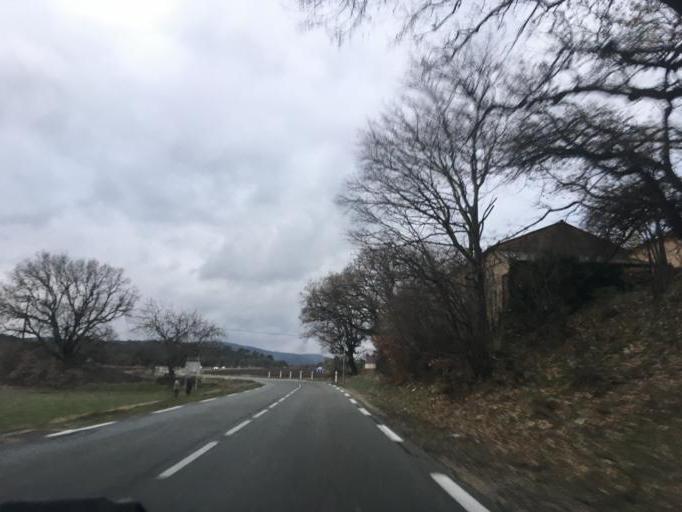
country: FR
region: Provence-Alpes-Cote d'Azur
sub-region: Departement du Var
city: Besse-sur-Issole
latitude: 43.3581
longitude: 6.1948
